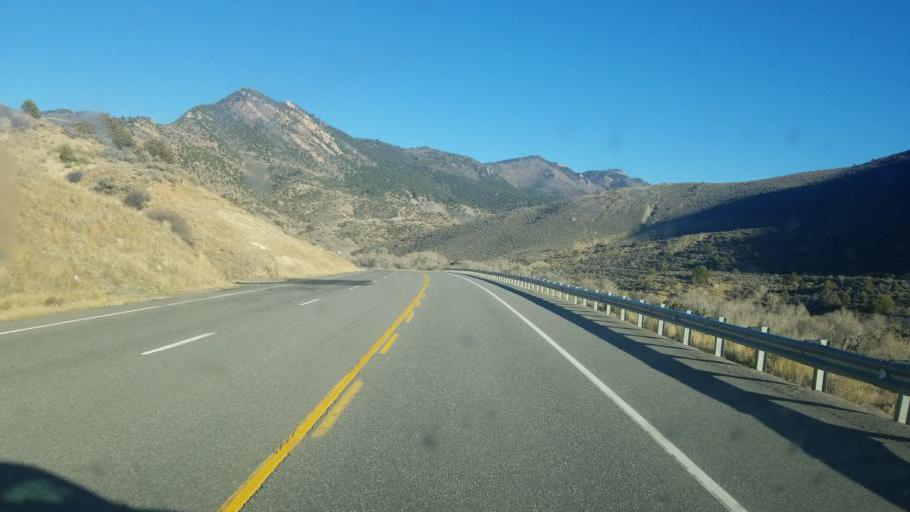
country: US
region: Colorado
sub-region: Montrose County
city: Montrose
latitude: 38.4408
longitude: -107.5702
